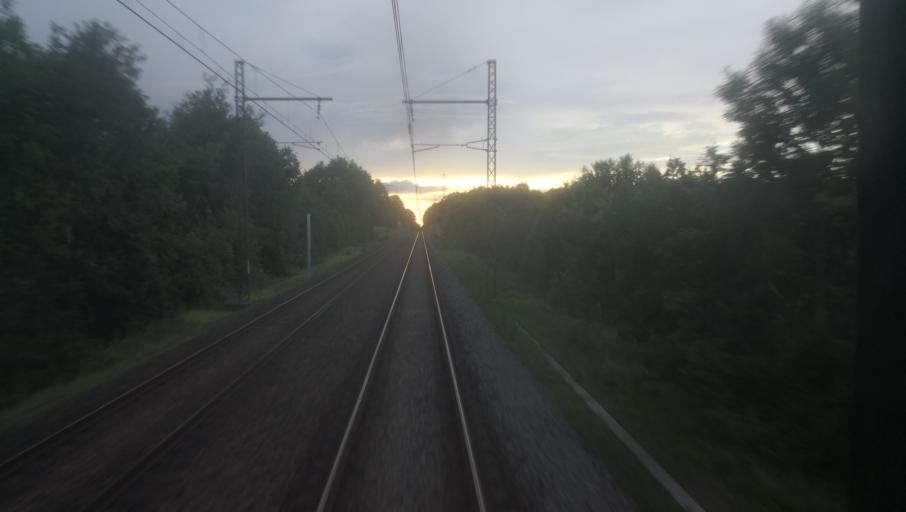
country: FR
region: Limousin
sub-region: Departement de la Haute-Vienne
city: Bessines-sur-Gartempe
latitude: 46.1382
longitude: 1.4295
